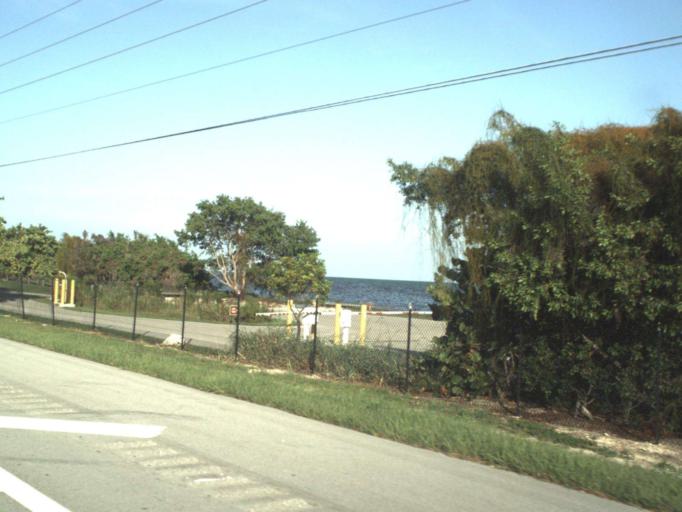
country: US
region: Florida
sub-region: Monroe County
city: Islamorada
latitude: 24.8107
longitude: -80.8294
